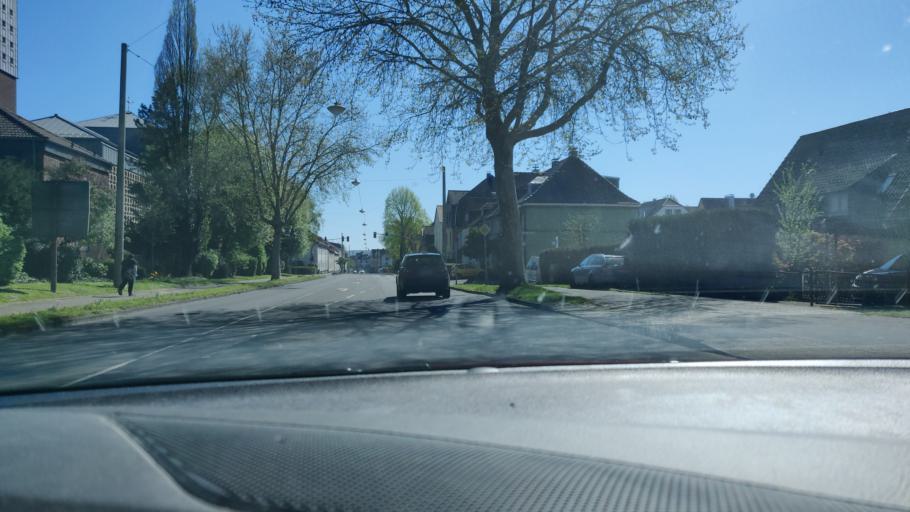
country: DE
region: North Rhine-Westphalia
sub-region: Regierungsbezirk Dusseldorf
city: Mettmann
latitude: 51.2533
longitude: 6.9616
